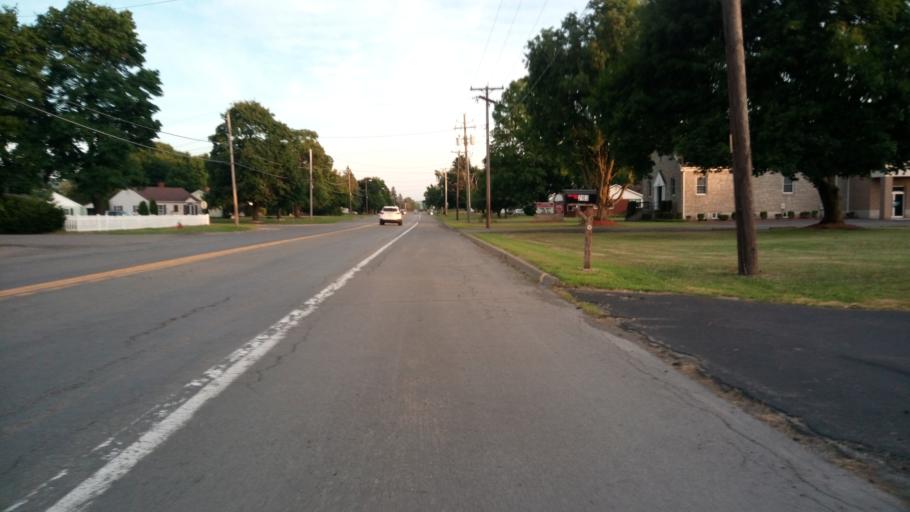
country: US
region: New York
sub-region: Chemung County
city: Horseheads
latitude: 42.1530
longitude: -76.8213
